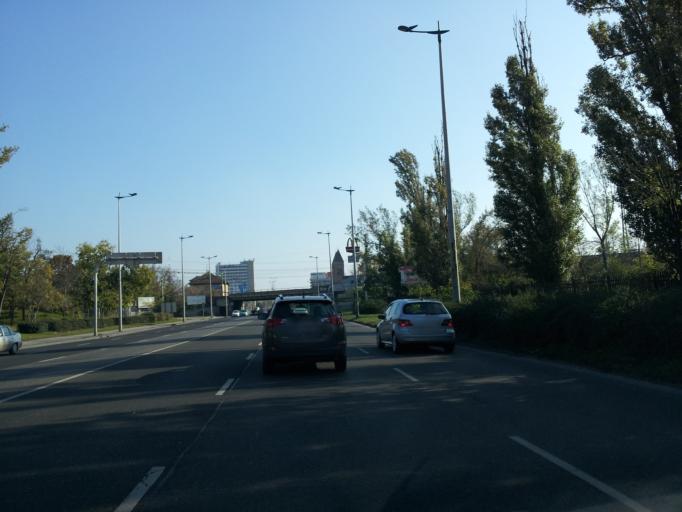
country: HU
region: Budapest
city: Budapest XX. keruelet
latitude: 47.4733
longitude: 19.1047
